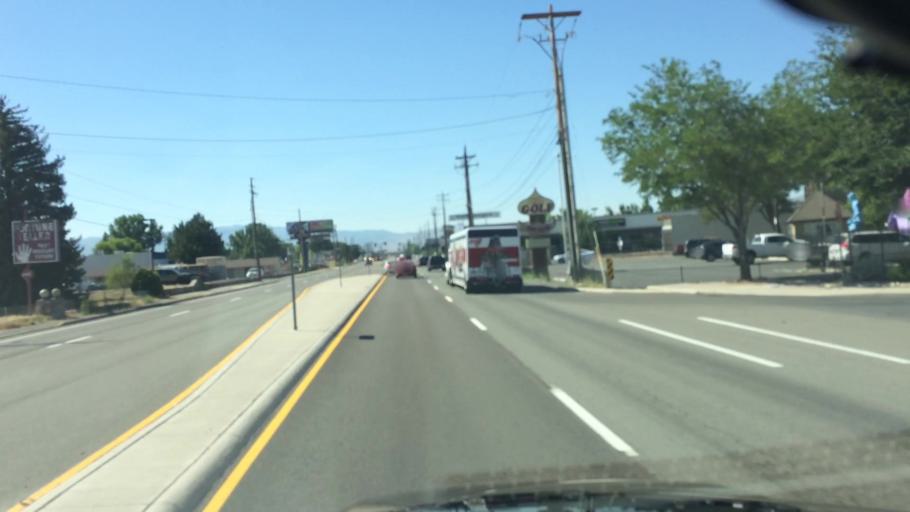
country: US
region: Nevada
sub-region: Washoe County
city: Reno
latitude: 39.4642
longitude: -119.7831
